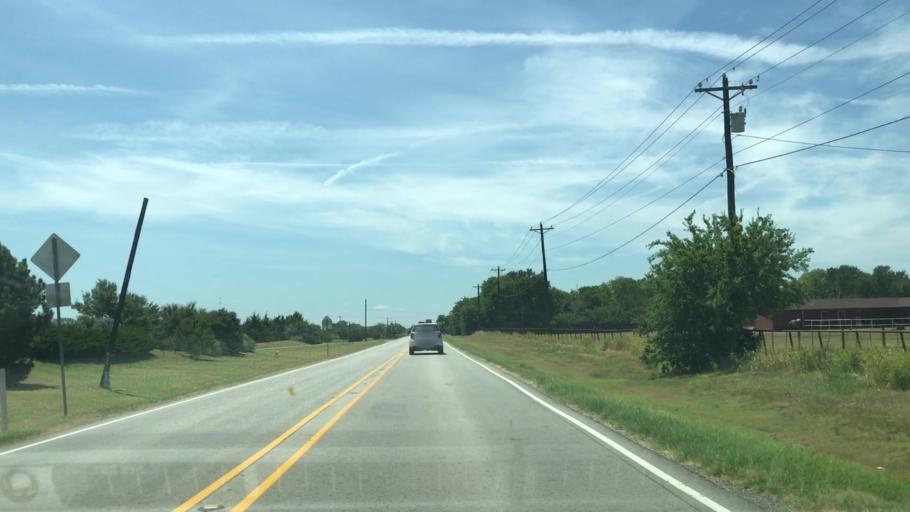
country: US
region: Texas
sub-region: Collin County
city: Lucas
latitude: 33.0893
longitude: -96.5909
